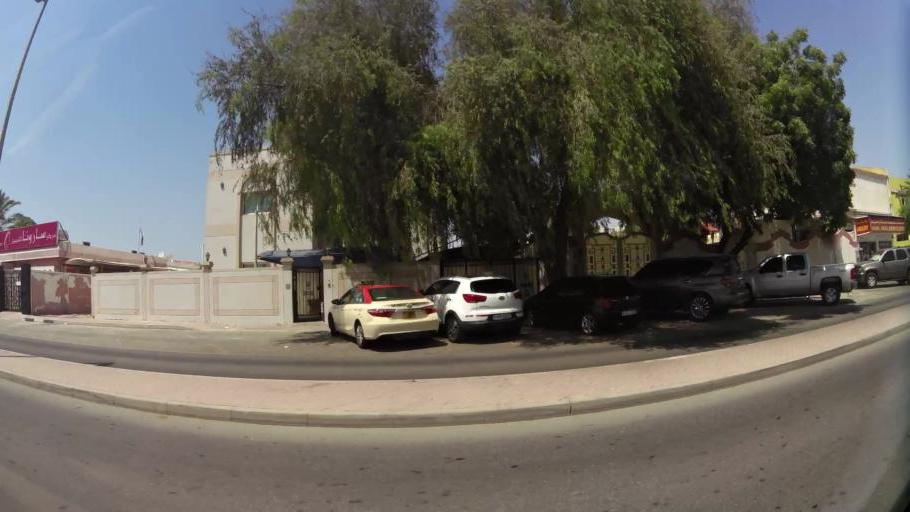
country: AE
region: Ash Shariqah
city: Sharjah
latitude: 25.2845
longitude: 55.3416
